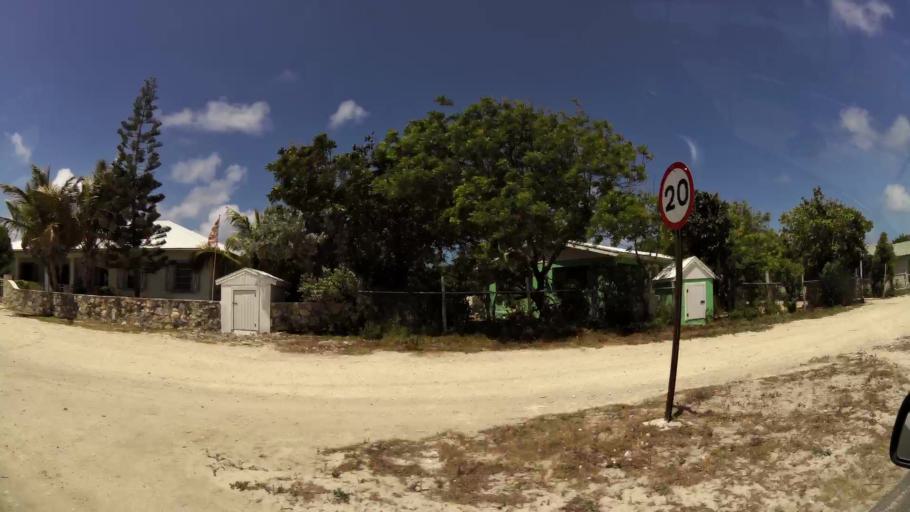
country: TC
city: Cockburn Town
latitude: 21.4506
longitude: -71.1461
